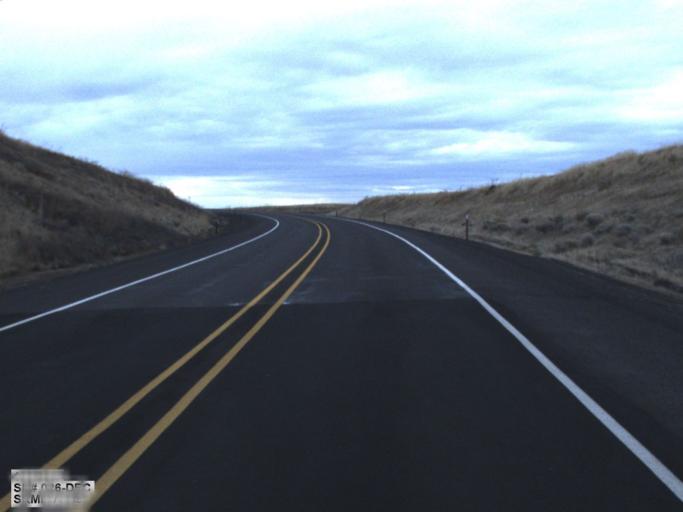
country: US
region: Washington
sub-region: Adams County
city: Ritzville
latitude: 46.7943
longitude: -118.3925
